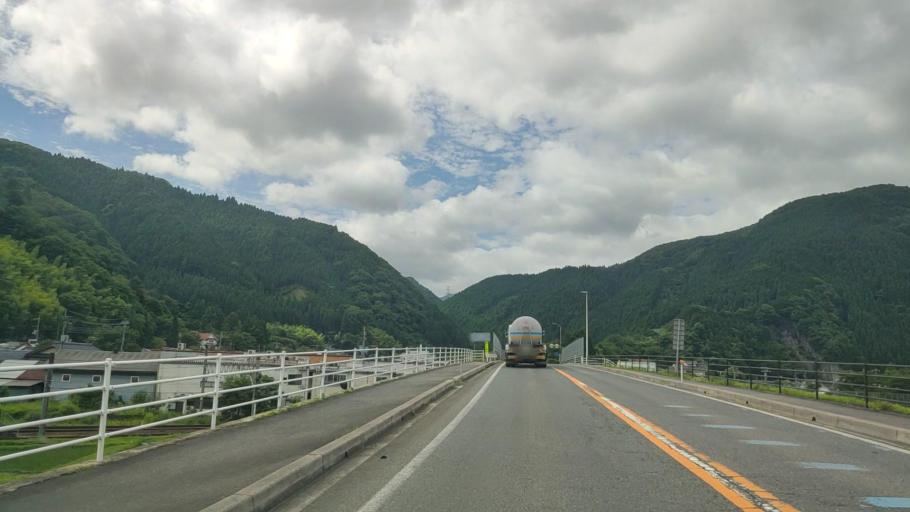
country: JP
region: Tottori
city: Yonago
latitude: 35.2413
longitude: 133.4403
